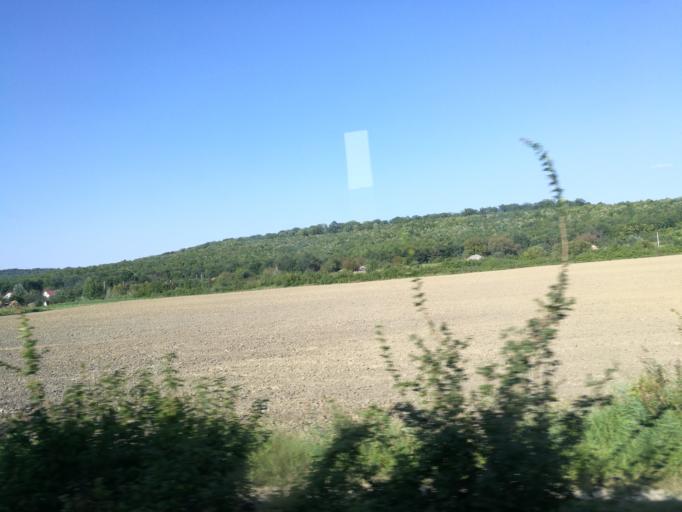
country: RO
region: Iasi
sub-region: Comuna Scanteia
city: Scanteia
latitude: 46.9555
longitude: 27.5606
